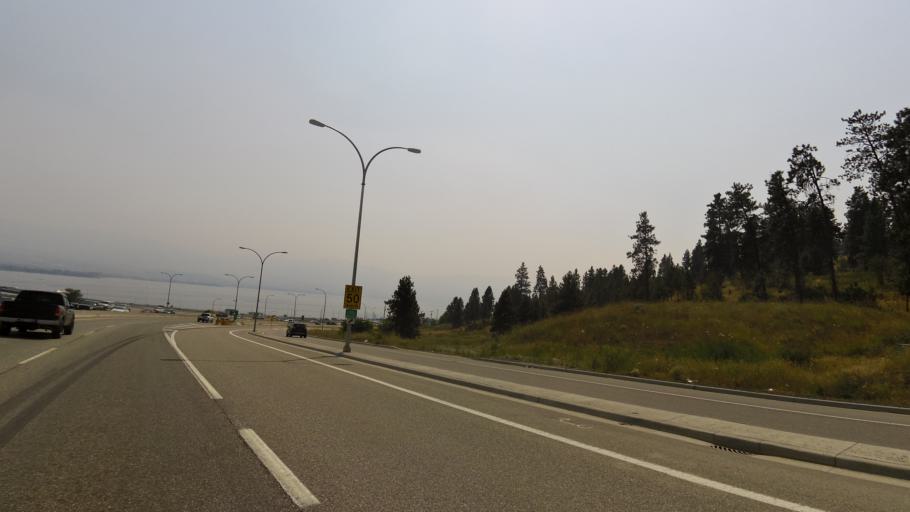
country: CA
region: British Columbia
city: Kelowna
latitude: 49.8826
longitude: -119.5251
